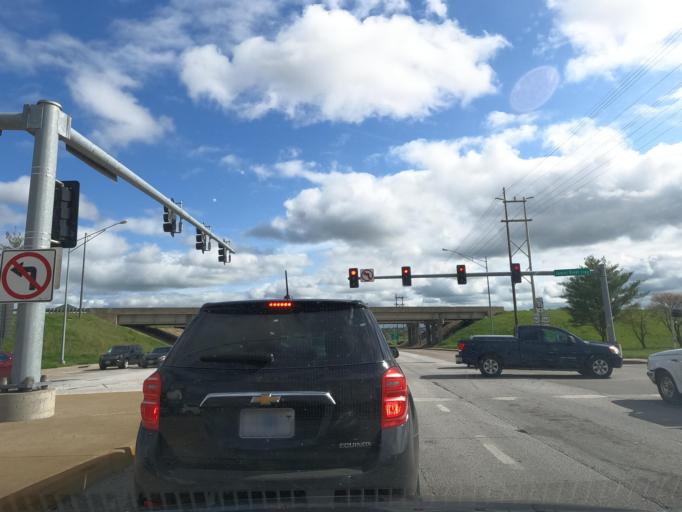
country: US
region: Missouri
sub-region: Greene County
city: Battlefield
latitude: 37.1372
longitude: -93.2964
